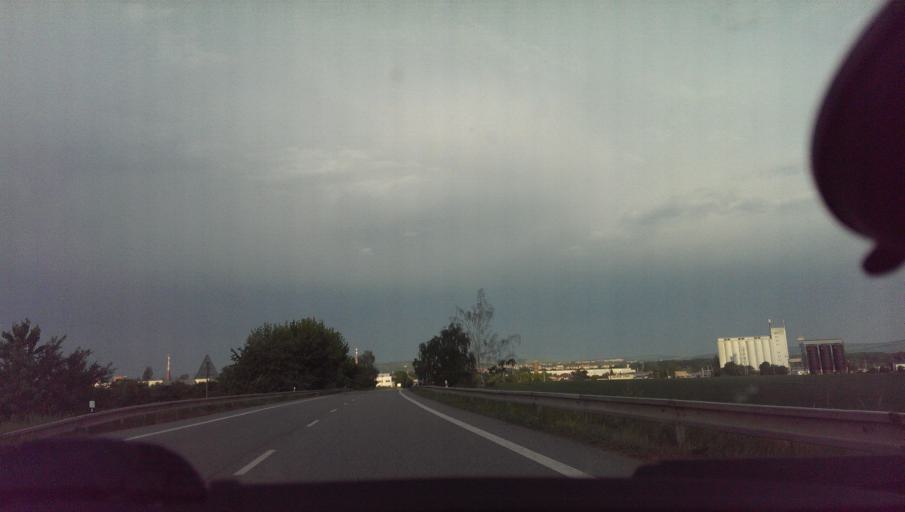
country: CZ
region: Zlin
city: Zlechov
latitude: 49.0740
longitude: 17.4044
